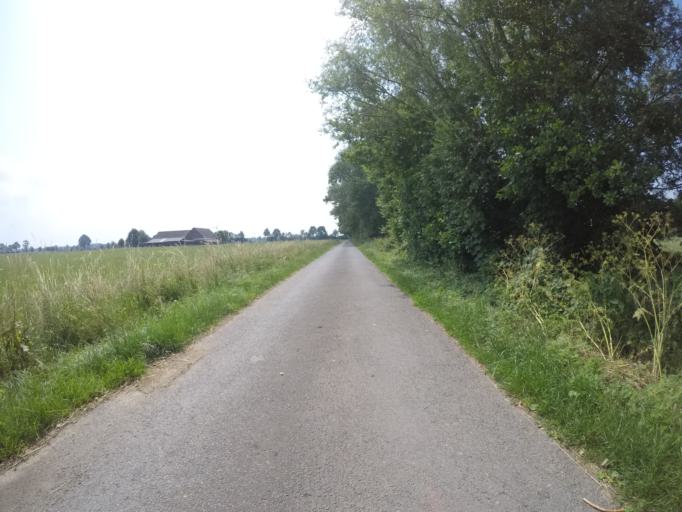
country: DE
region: North Rhine-Westphalia
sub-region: Regierungsbezirk Munster
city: Isselburg
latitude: 51.8450
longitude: 6.5215
